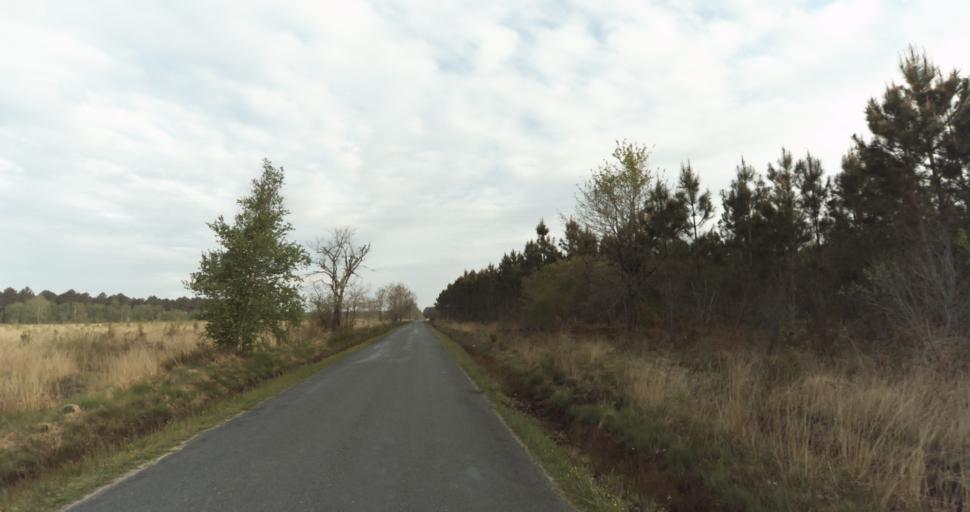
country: FR
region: Aquitaine
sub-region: Departement de la Gironde
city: Saint-Aubin-de-Medoc
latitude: 44.7849
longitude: -0.7509
